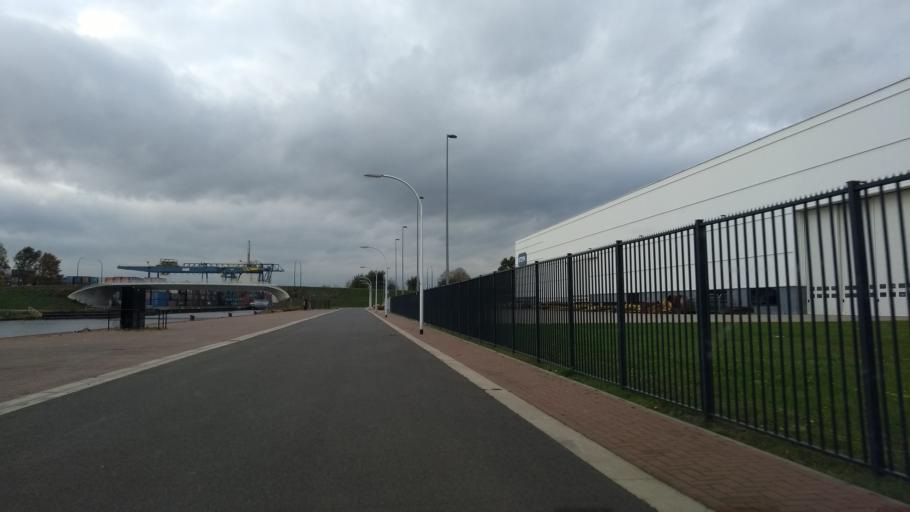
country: NL
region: Overijssel
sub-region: Gemeente Hengelo
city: Hengelo
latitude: 52.2479
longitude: 6.7927
